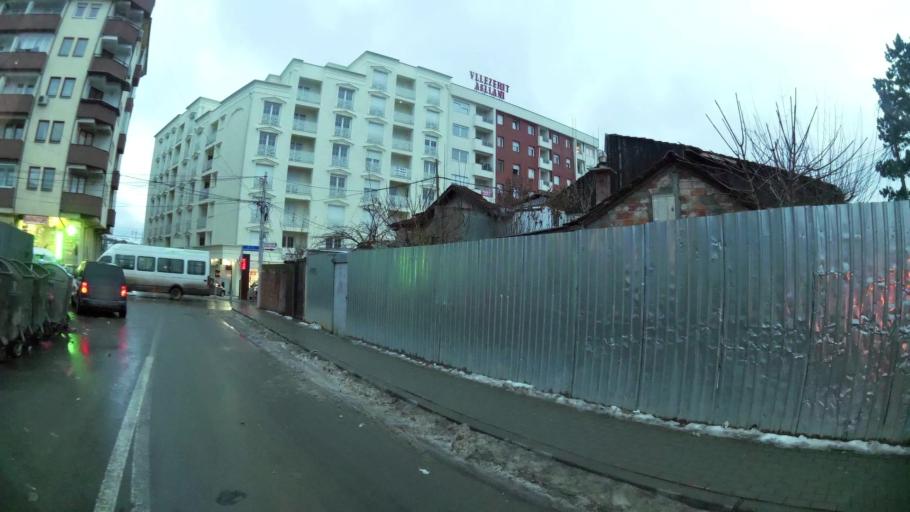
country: XK
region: Pristina
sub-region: Komuna e Prishtines
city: Pristina
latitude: 42.6436
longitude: 21.1664
